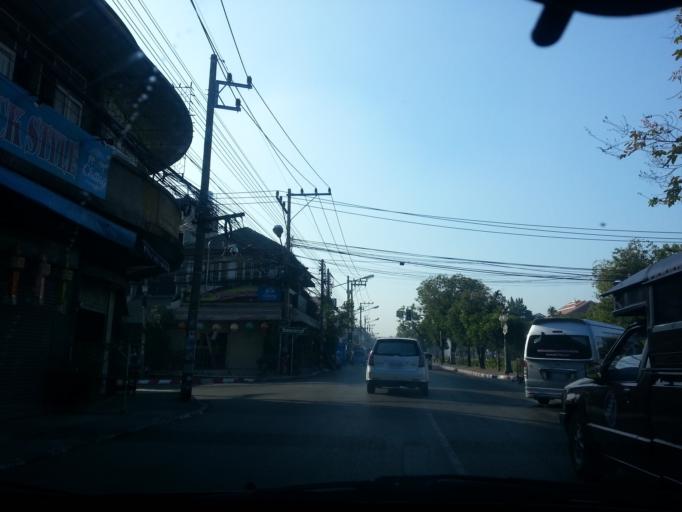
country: TH
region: Chiang Mai
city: Chiang Mai
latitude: 18.7853
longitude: 98.9934
